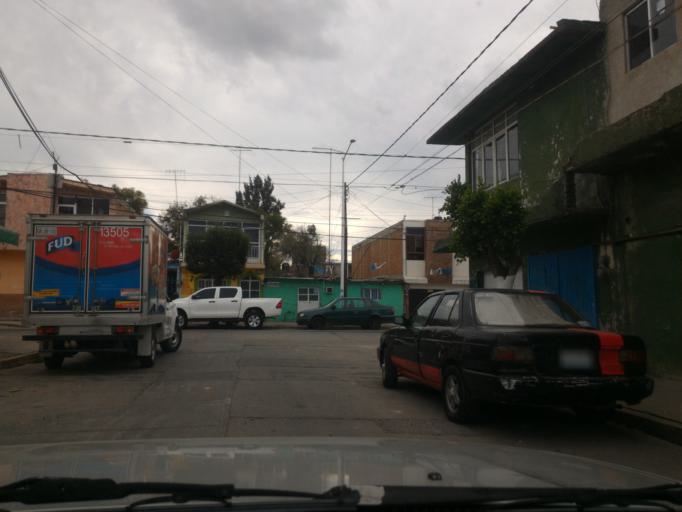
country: MX
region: Guanajuato
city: San Francisco del Rincon
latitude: 21.0249
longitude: -101.8619
